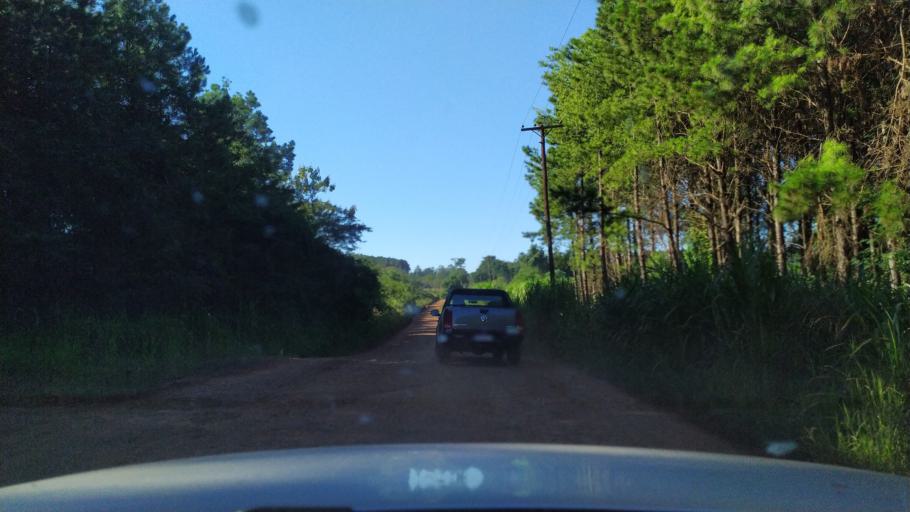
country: AR
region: Misiones
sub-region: Departamento de Montecarlo
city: Montecarlo
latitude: -26.6126
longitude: -54.6984
